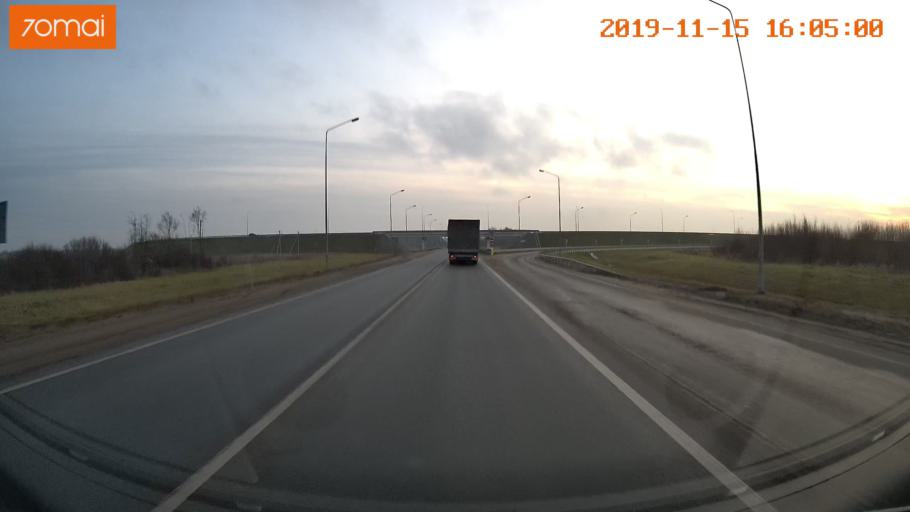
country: RU
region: Jaroslavl
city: Yaroslavl
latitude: 57.7410
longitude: 39.8972
